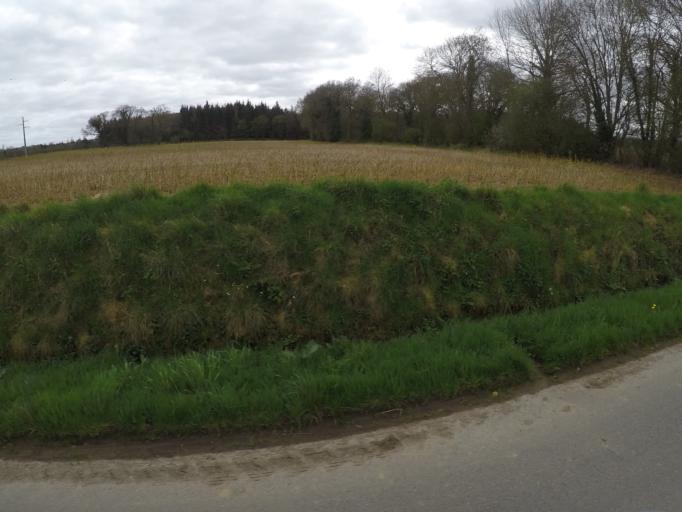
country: FR
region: Brittany
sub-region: Departement des Cotes-d'Armor
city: Plouha
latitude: 48.6563
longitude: -2.9237
